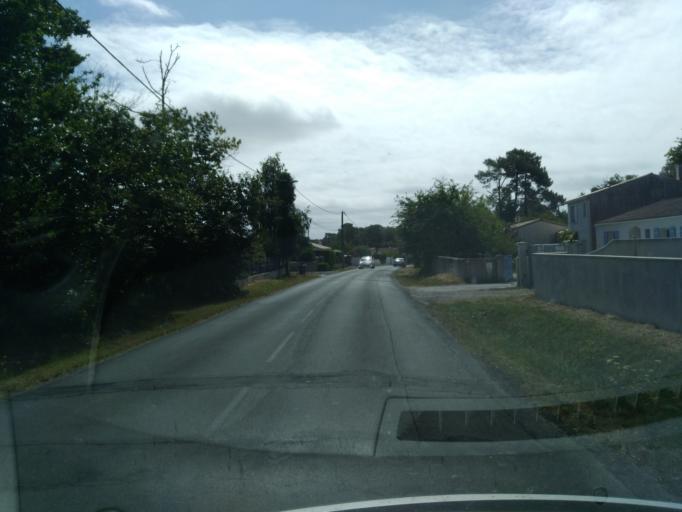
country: FR
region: Poitou-Charentes
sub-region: Departement de la Charente-Maritime
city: Saint-Palais-sur-Mer
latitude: 45.6679
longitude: -1.0814
